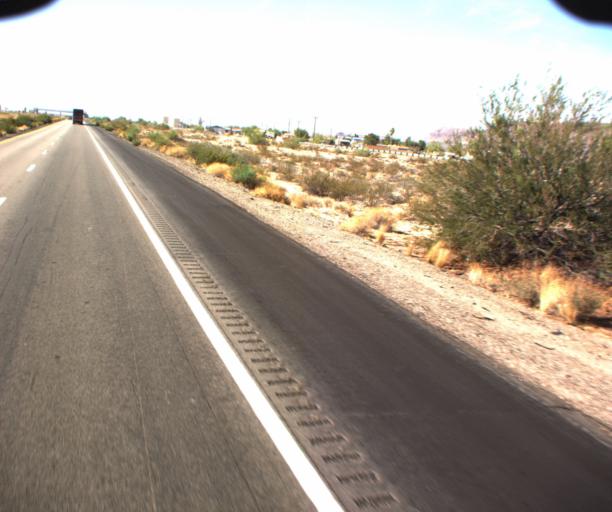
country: US
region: Arizona
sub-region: Mohave County
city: Kingman
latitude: 34.8787
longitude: -114.1483
